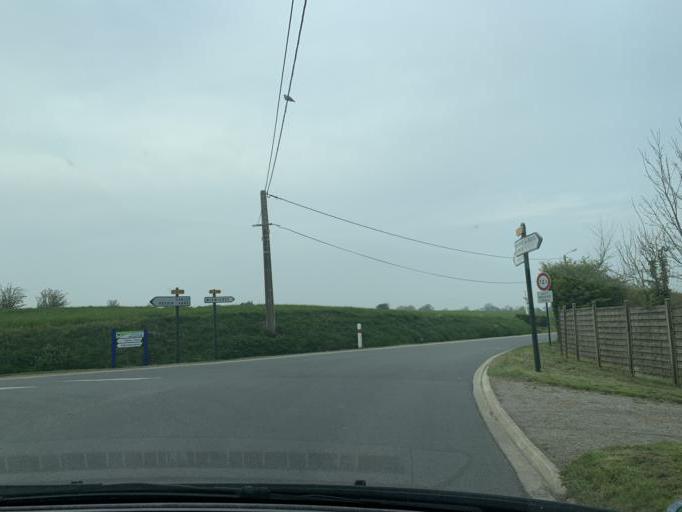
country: FR
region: Nord-Pas-de-Calais
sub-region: Departement du Pas-de-Calais
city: Samer
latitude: 50.6657
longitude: 1.7488
